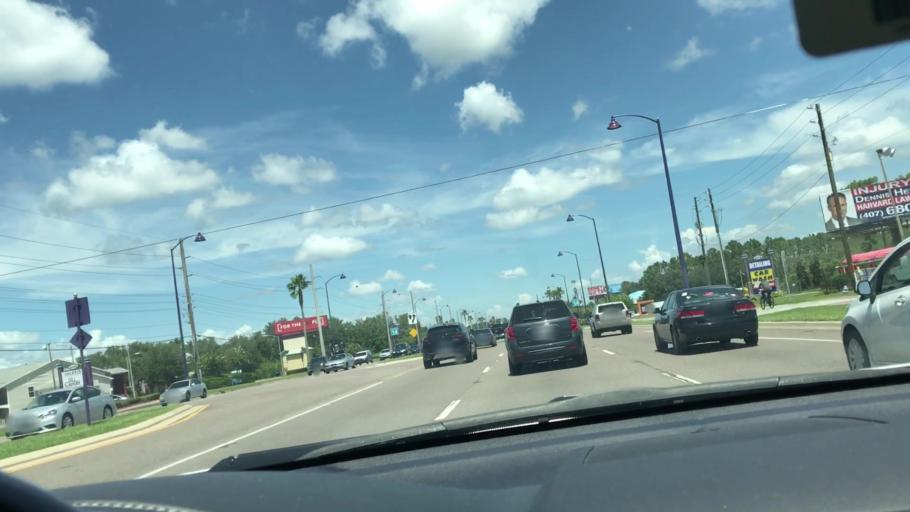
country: US
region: Florida
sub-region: Osceola County
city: Kissimmee
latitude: 28.3103
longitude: -81.4655
